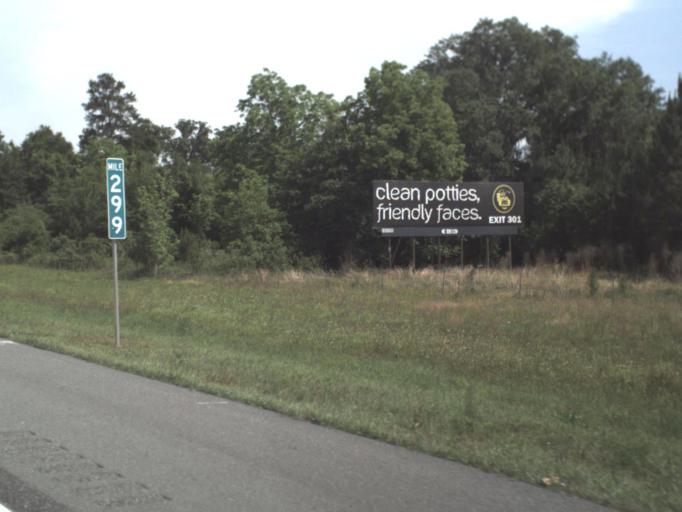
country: US
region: Florida
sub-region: Columbia County
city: Five Points
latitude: 30.2523
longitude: -82.7116
